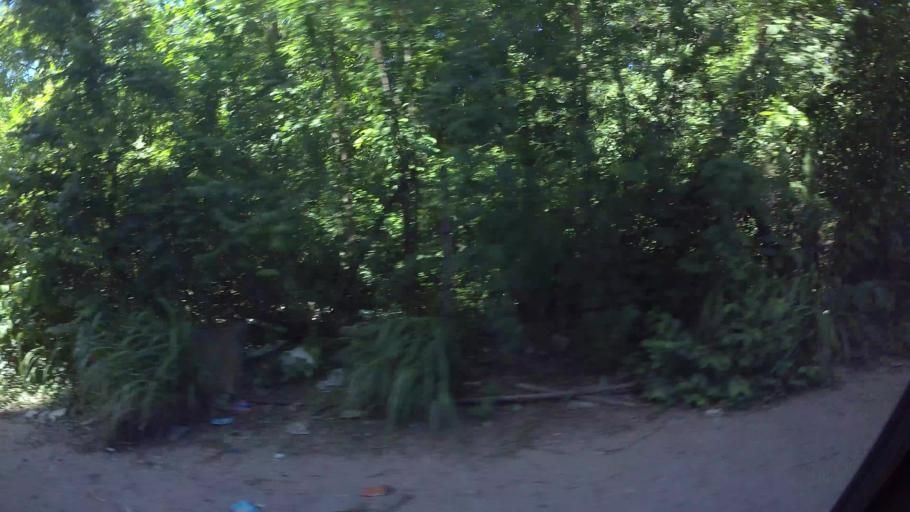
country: TH
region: Chon Buri
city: Phatthaya
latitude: 12.9189
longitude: 100.8651
